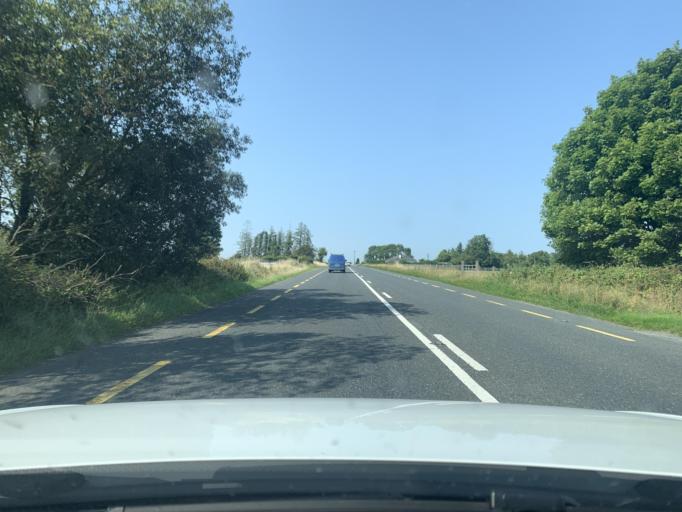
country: IE
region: Leinster
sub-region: An Iarmhi
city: Athlone
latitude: 53.5063
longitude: -8.0459
